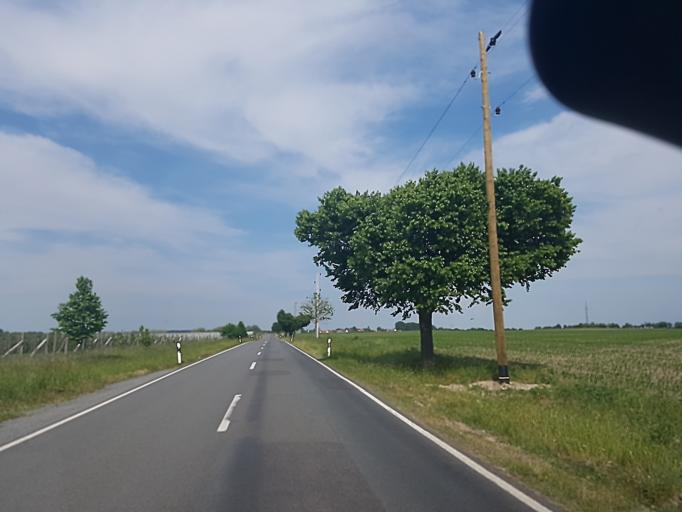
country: DE
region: Brandenburg
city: Gorzke
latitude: 52.1025
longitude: 12.3534
